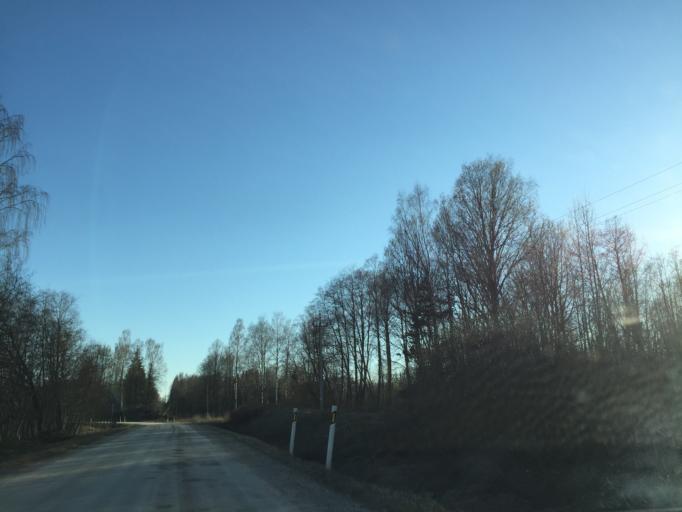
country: EE
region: Ida-Virumaa
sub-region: Sillamaee linn
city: Sillamae
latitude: 59.1364
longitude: 27.8110
